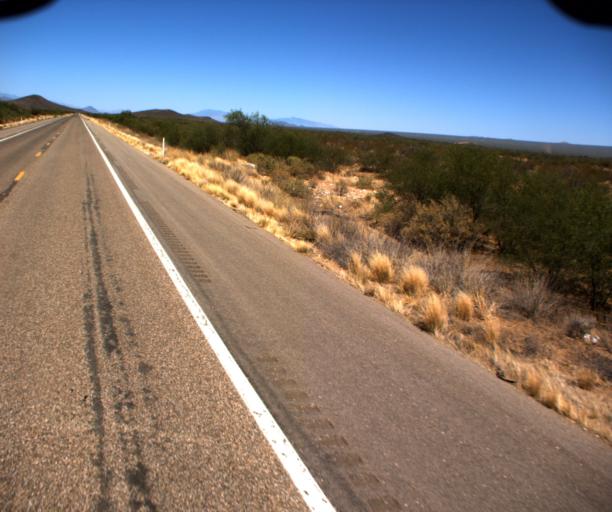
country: US
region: Arizona
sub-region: Pima County
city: Three Points
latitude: 32.0480
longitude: -111.4265
